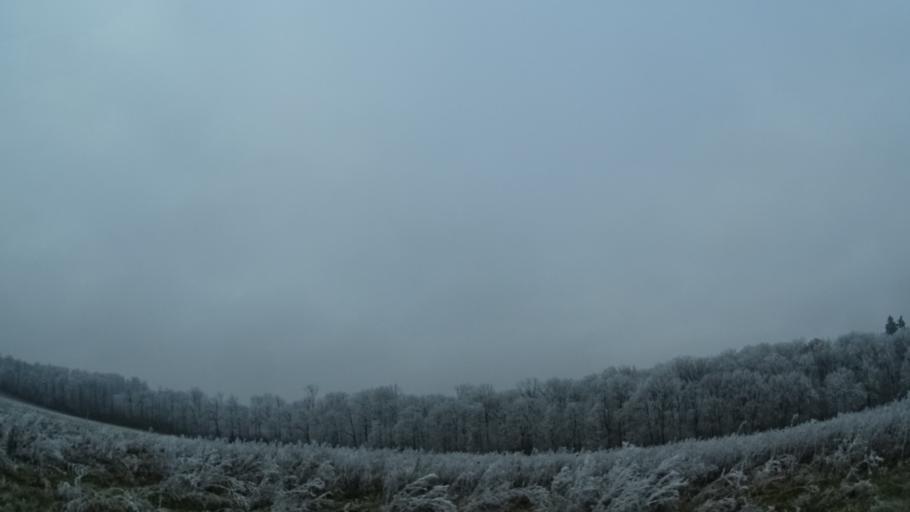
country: DE
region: Baden-Wuerttemberg
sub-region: Regierungsbezirk Stuttgart
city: Krautheim
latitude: 49.4362
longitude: 9.5864
